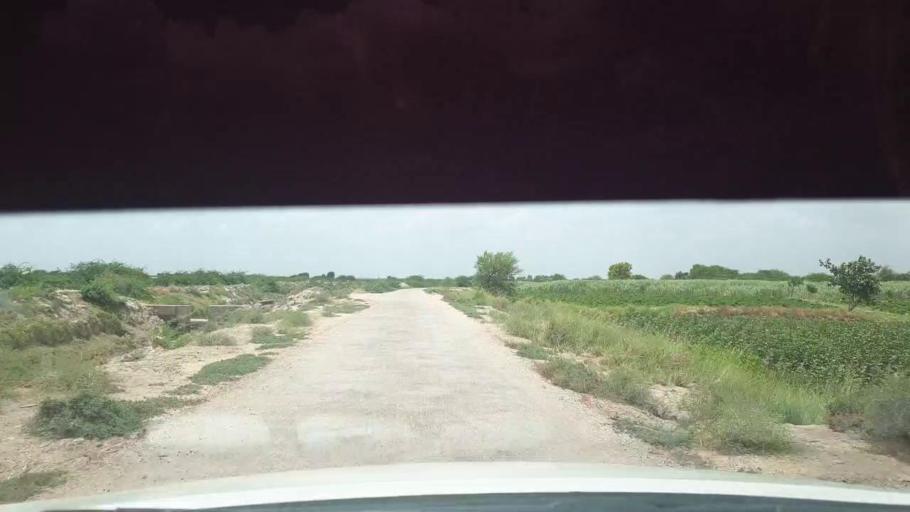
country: PK
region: Sindh
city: Kadhan
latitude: 24.5412
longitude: 69.1228
